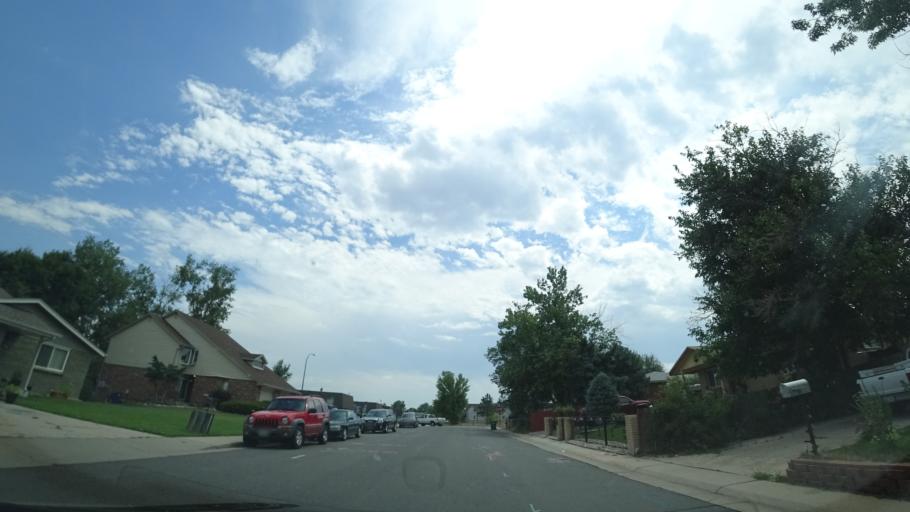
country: US
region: Colorado
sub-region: Jefferson County
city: Lakewood
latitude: 39.6973
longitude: -105.0751
